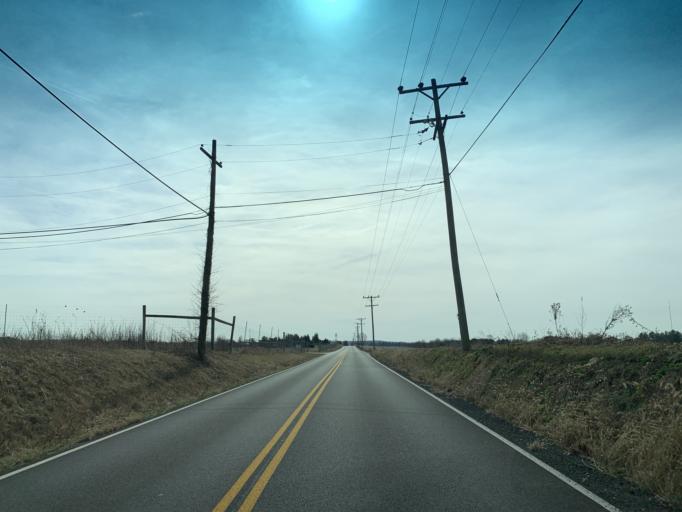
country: US
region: Maryland
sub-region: Frederick County
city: Adamstown
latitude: 39.3012
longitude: -77.4642
